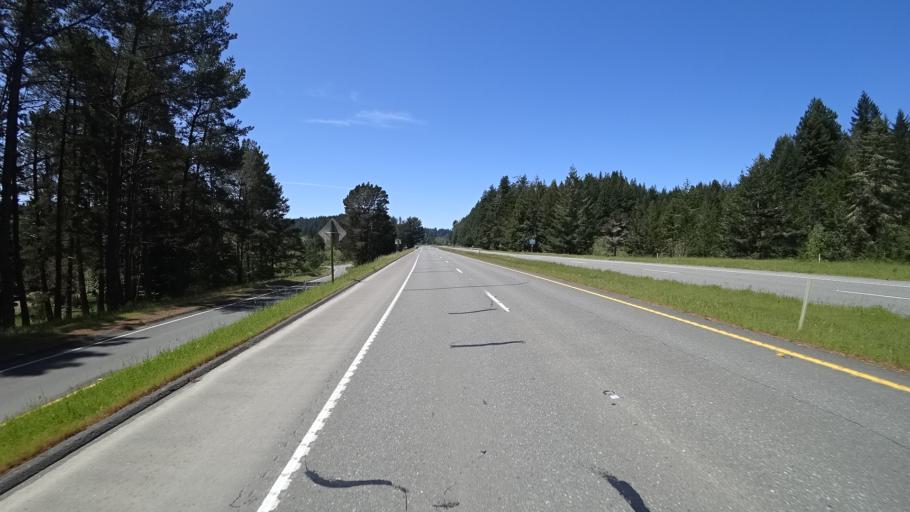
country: US
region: California
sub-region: Humboldt County
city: Blue Lake
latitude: 40.9069
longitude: -124.0351
